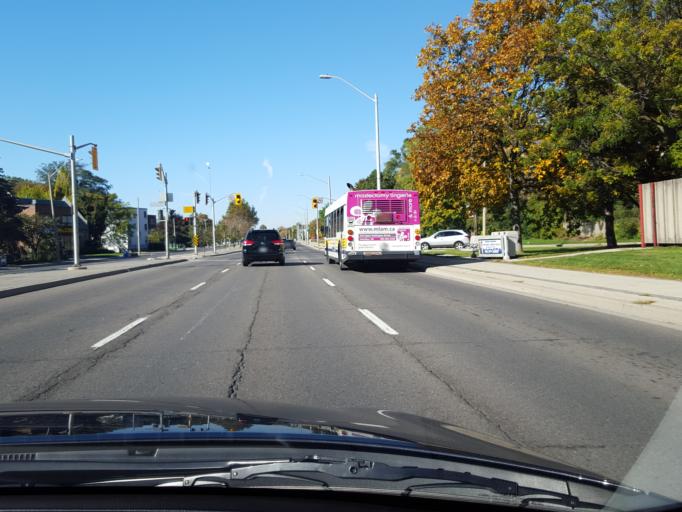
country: CA
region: Ontario
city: Hamilton
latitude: 43.2580
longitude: -79.9132
